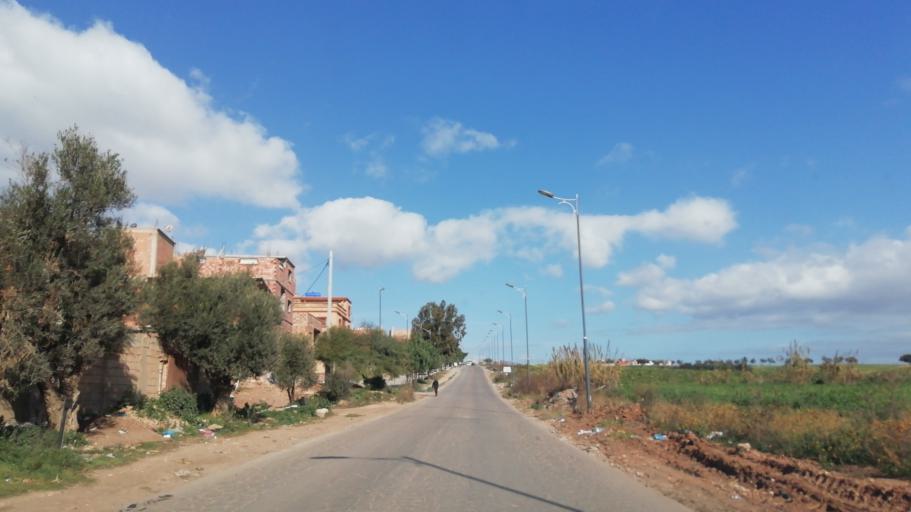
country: DZ
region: Oran
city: Es Senia
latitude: 35.6285
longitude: -0.6616
